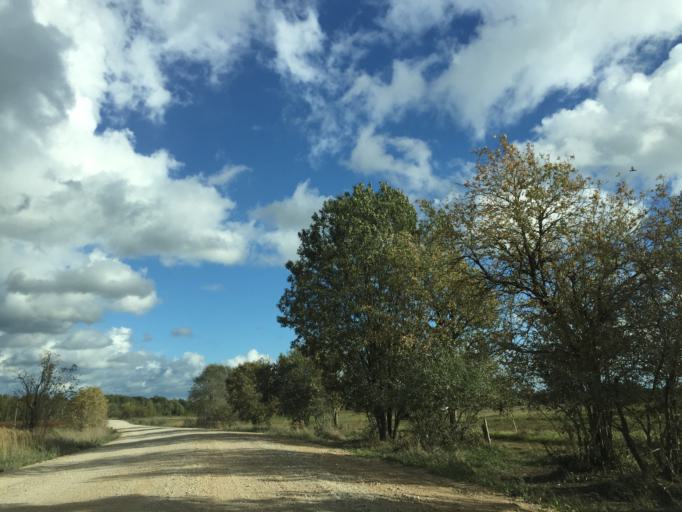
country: LV
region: Malpils
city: Malpils
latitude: 57.0156
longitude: 24.9977
